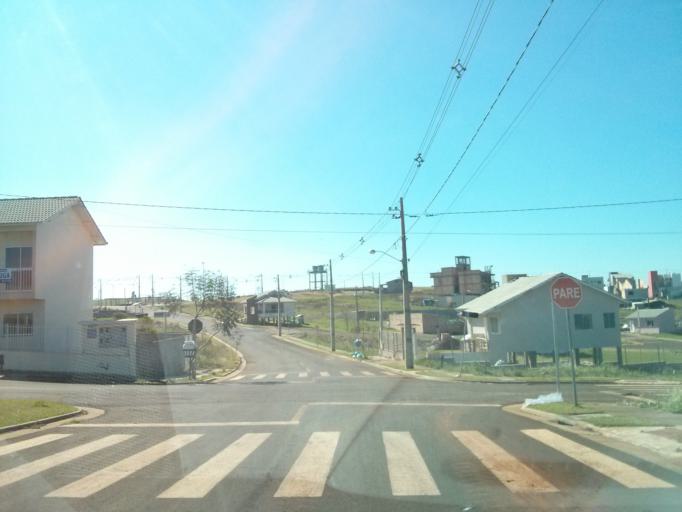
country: BR
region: Santa Catarina
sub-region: Chapeco
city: Chapeco
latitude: -27.0916
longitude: -52.7128
